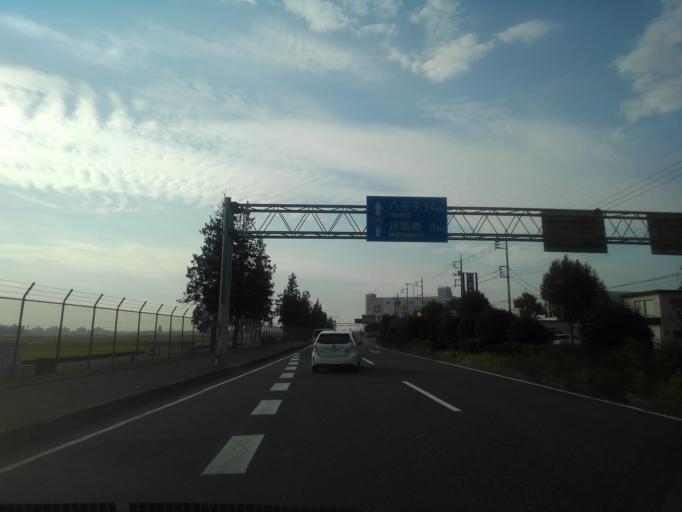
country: JP
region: Tokyo
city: Fussa
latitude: 35.7617
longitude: 139.3422
